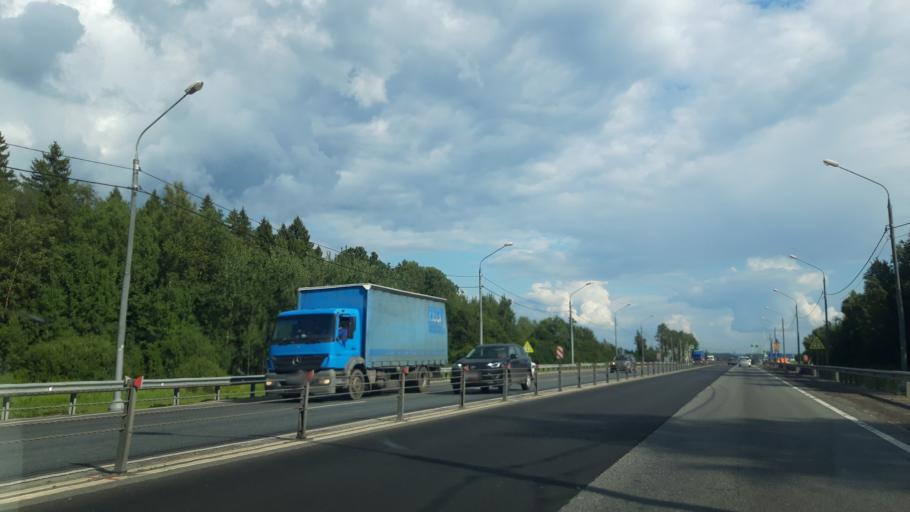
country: RU
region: Moskovskaya
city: Solnechnogorsk
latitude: 56.2473
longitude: 36.8812
